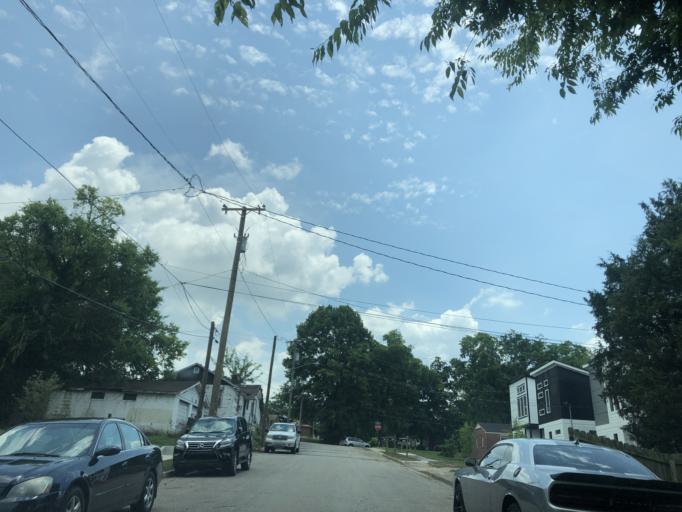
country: US
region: Tennessee
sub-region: Davidson County
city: Nashville
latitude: 36.1628
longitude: -86.8220
